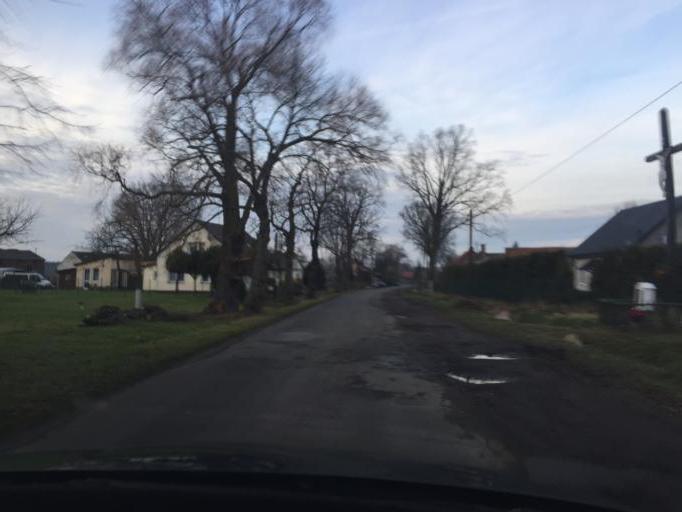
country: PL
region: Lubusz
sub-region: Powiat zielonogorski
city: Ochla
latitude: 51.8037
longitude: 15.4924
